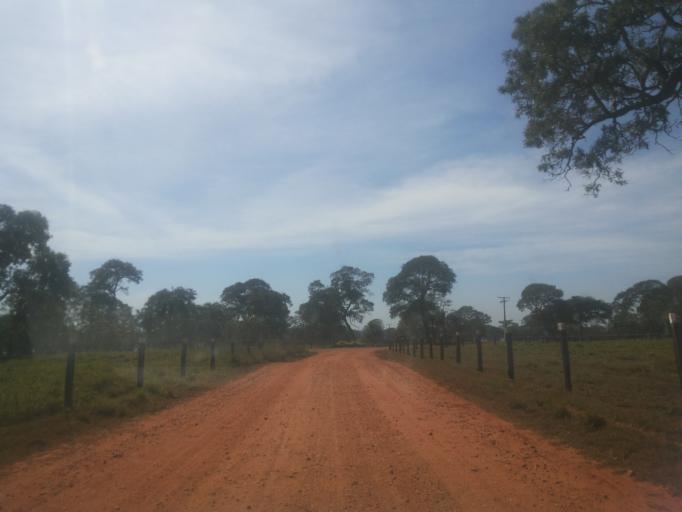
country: BR
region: Minas Gerais
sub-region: Santa Vitoria
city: Santa Vitoria
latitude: -19.0054
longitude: -50.4269
